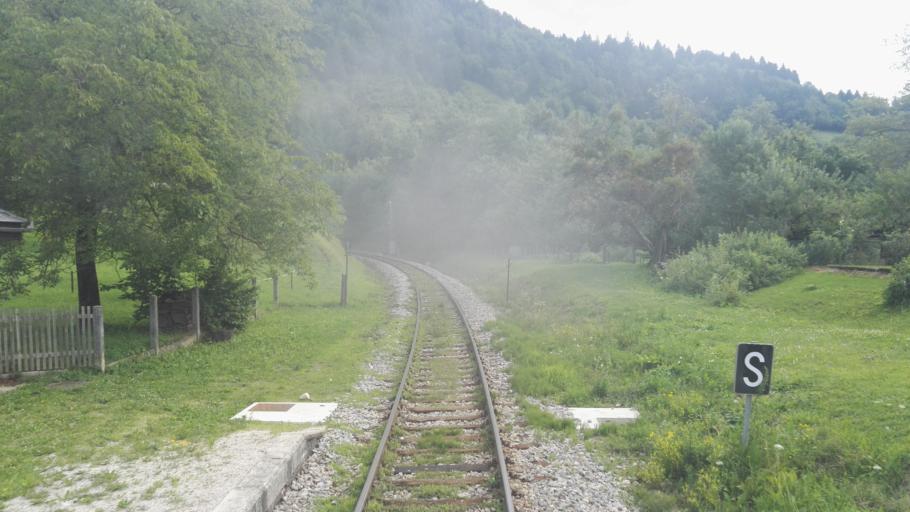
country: SI
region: Bled
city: Zasip
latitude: 46.3876
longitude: 14.0944
